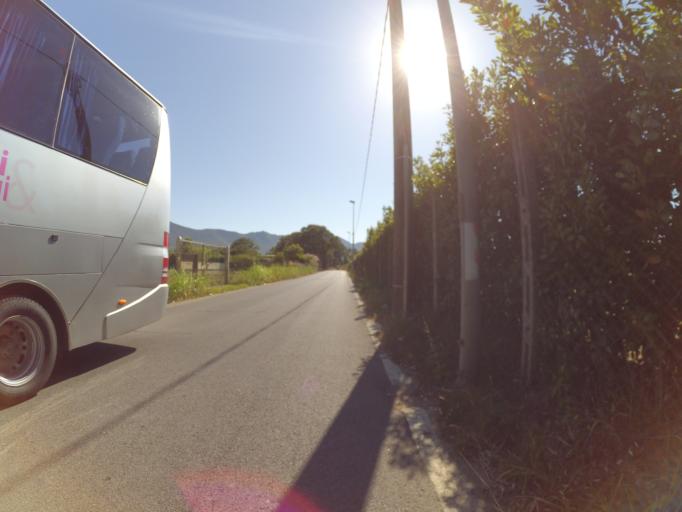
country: IT
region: Latium
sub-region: Provincia di Latina
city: San Felice Circeo
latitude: 41.2515
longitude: 13.0905
